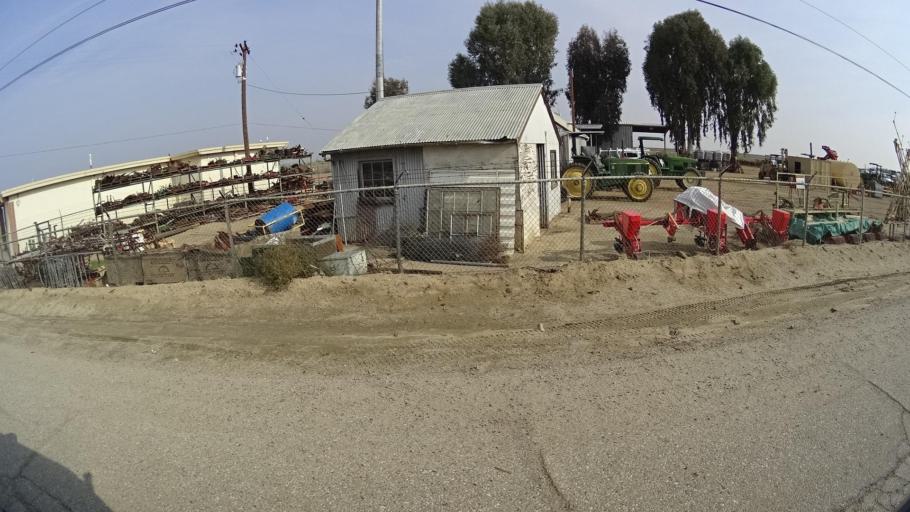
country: US
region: California
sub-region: Kern County
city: Weedpatch
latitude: 35.0587
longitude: -118.9675
